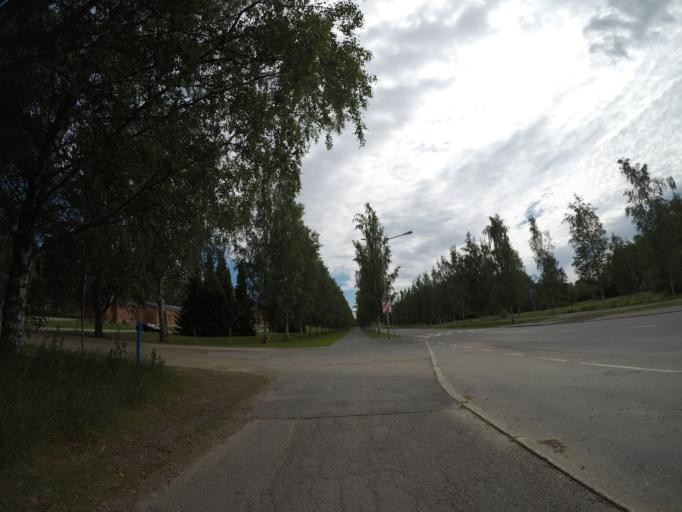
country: FI
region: Haeme
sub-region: Haemeenlinna
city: Haemeenlinna
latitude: 61.0063
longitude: 24.4530
